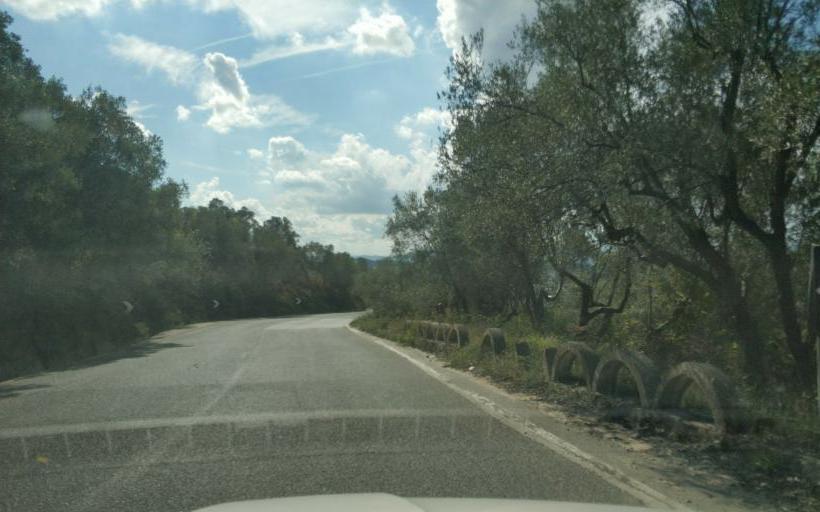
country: AL
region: Durres
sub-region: Rrethi i Krujes
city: Kruje
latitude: 41.4843
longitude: 19.7660
